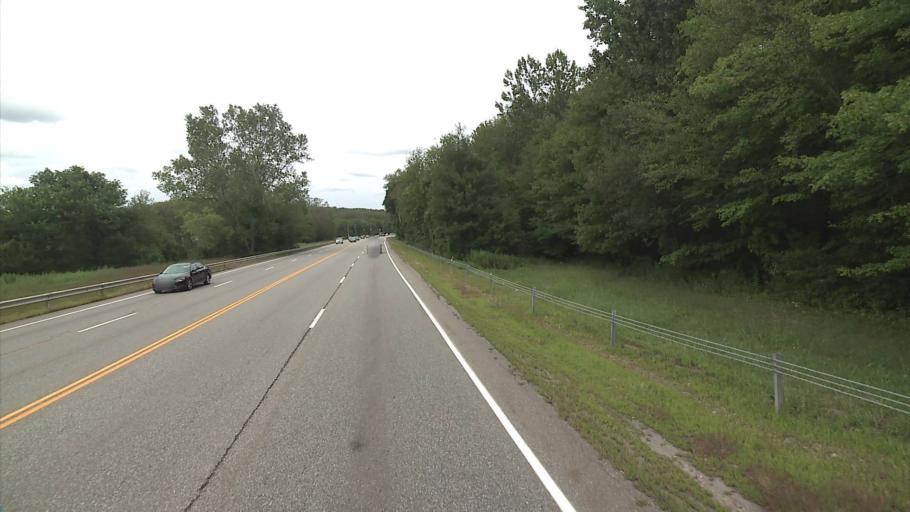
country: US
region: Connecticut
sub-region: New London County
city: Central Waterford
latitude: 41.3827
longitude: -72.1548
